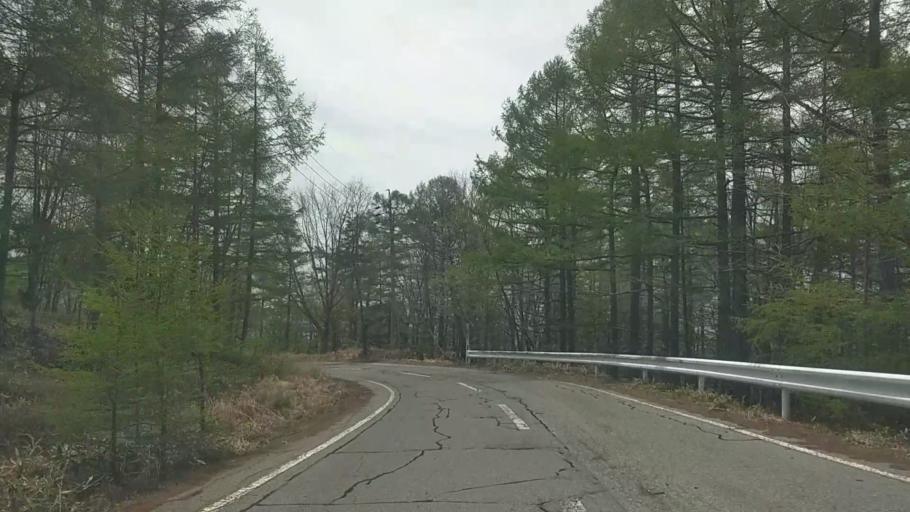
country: JP
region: Nagano
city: Chino
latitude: 36.0518
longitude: 138.3101
